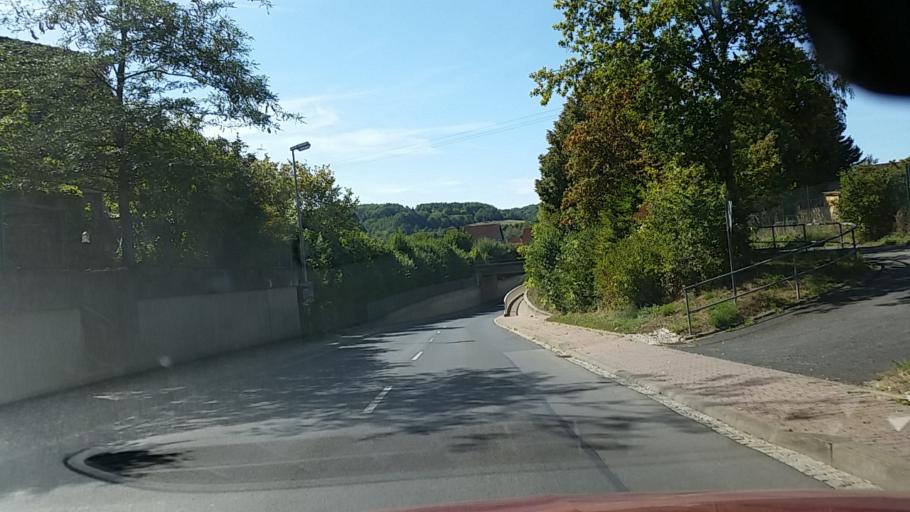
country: DE
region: Bavaria
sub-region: Regierungsbezirk Unterfranken
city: Himmelstadt
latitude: 49.9228
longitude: 9.8098
